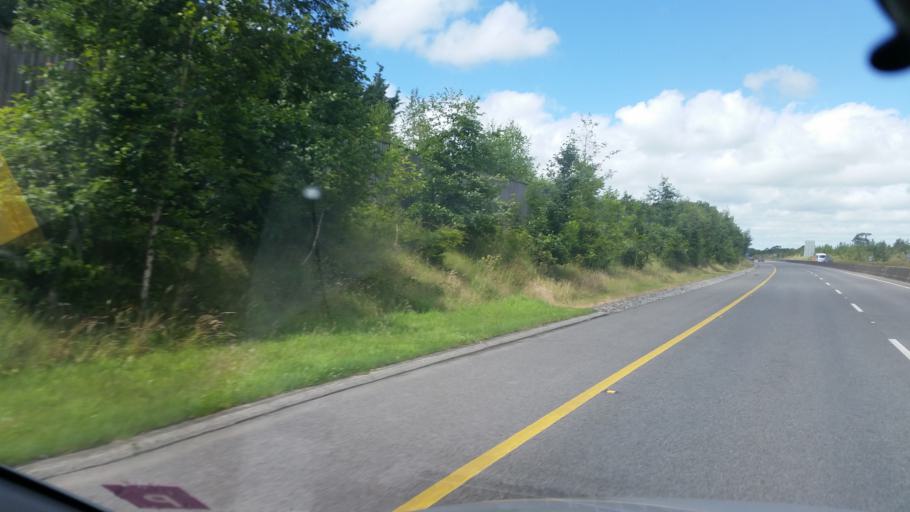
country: IE
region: Leinster
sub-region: An Mhi
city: Dunboyne
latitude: 53.4436
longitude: -6.4717
